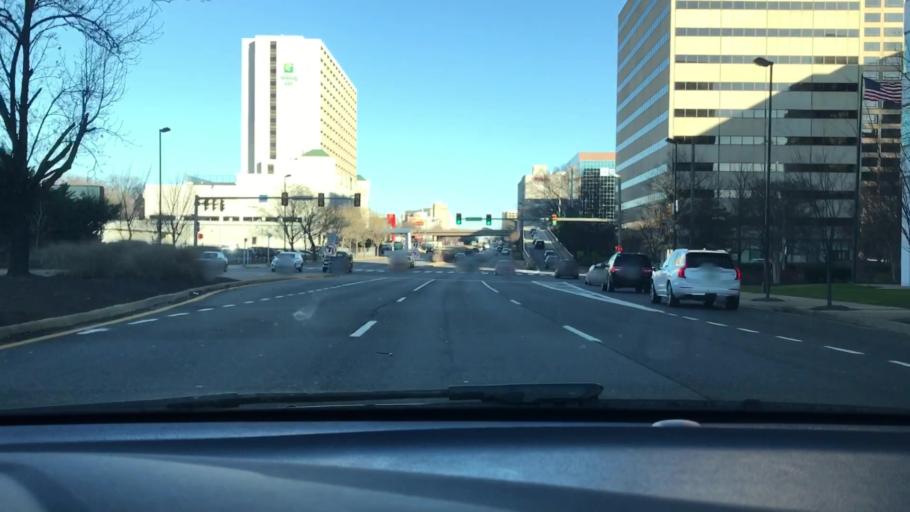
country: US
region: Virginia
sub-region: City of Alexandria
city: Alexandria
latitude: 38.8475
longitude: -77.0529
